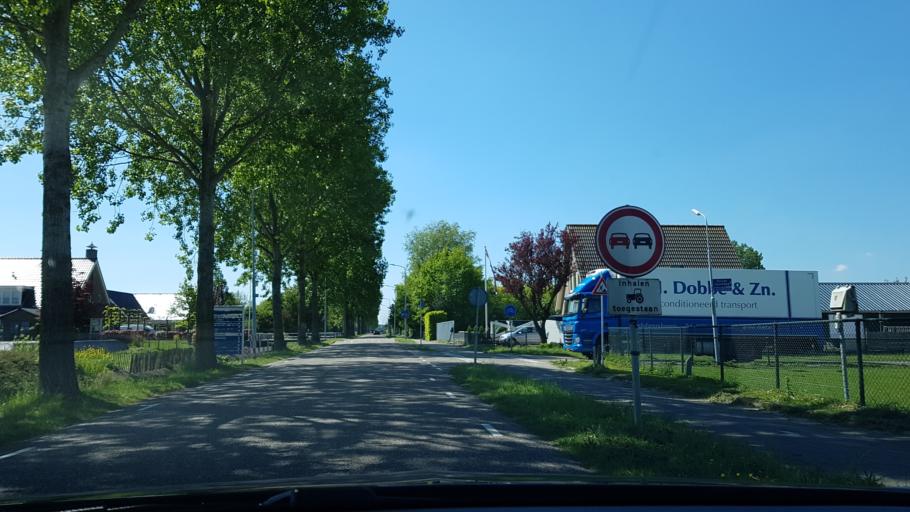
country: NL
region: South Holland
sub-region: Gemeente Kaag en Braassem
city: Leimuiden
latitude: 52.2492
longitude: 4.6910
